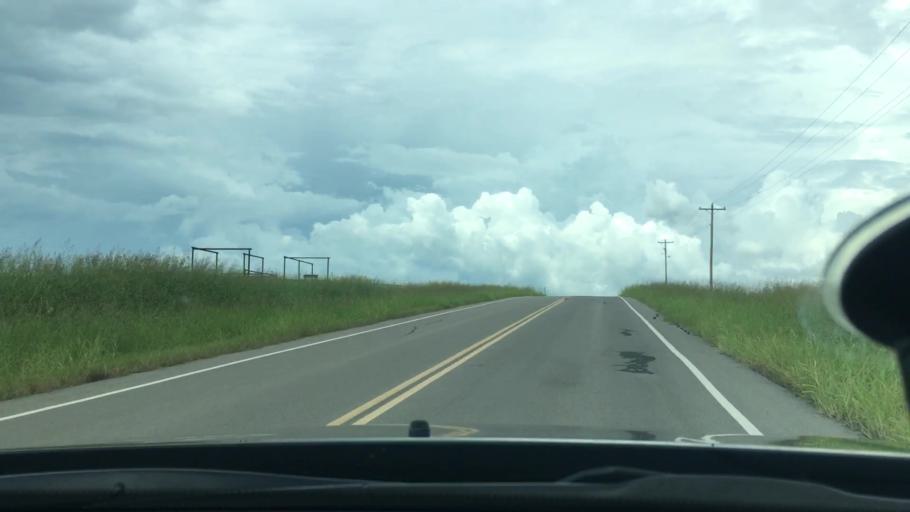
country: US
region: Oklahoma
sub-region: Garvin County
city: Stratford
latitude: 34.8155
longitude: -97.0554
